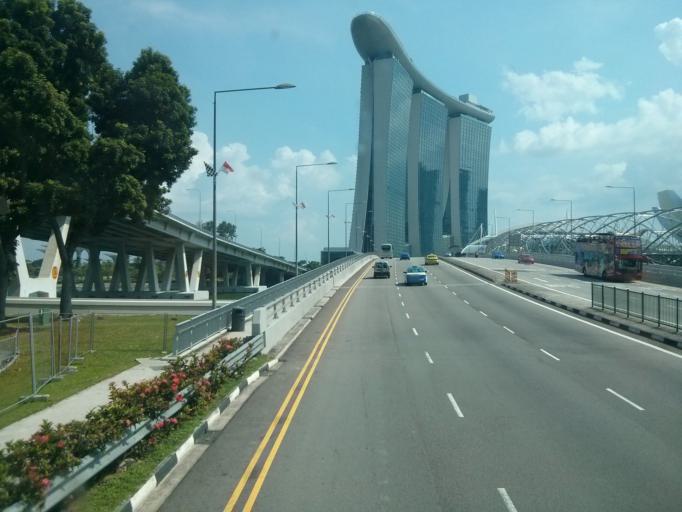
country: SG
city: Singapore
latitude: 1.2893
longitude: 103.8610
